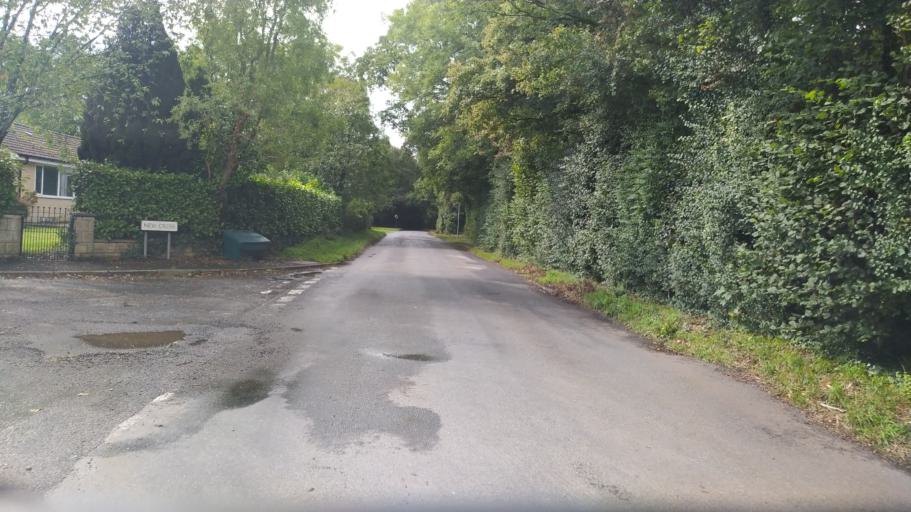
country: GB
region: England
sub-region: Dorset
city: Sherborne
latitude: 50.9182
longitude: -2.5069
